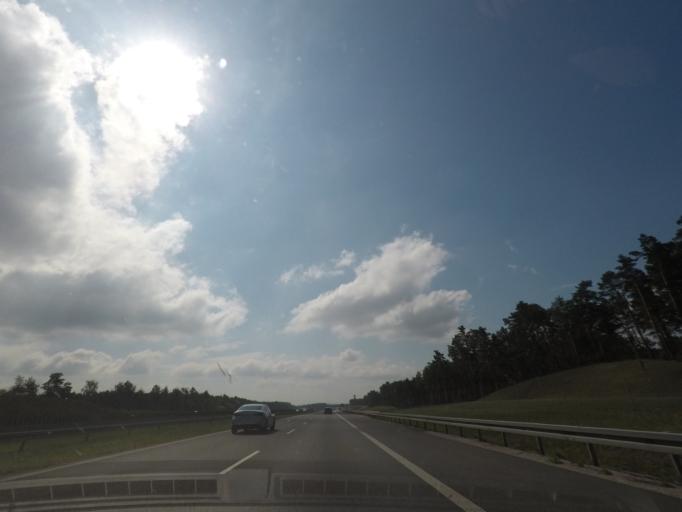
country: PL
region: Kujawsko-Pomorskie
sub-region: Powiat aleksandrowski
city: Aleksandrow Kujawski
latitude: 52.9128
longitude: 18.7165
